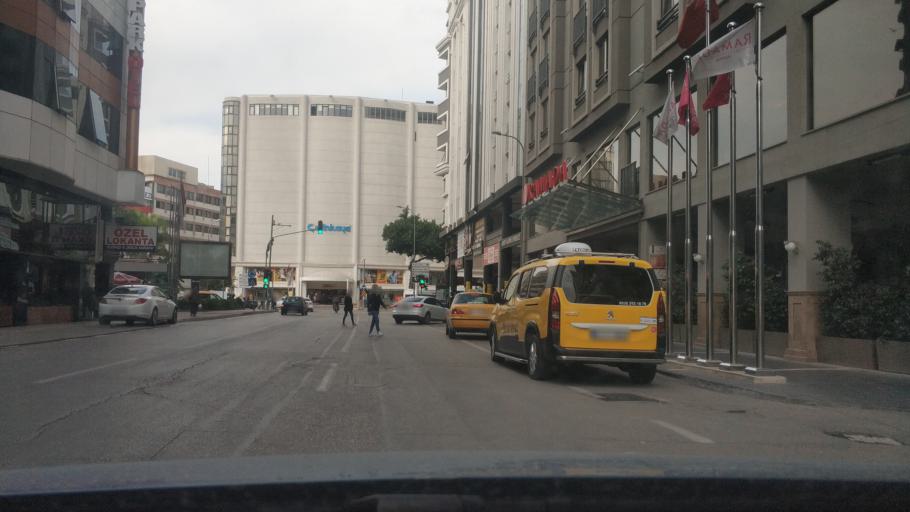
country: TR
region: Adana
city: Adana
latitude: 36.9900
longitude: 35.3224
